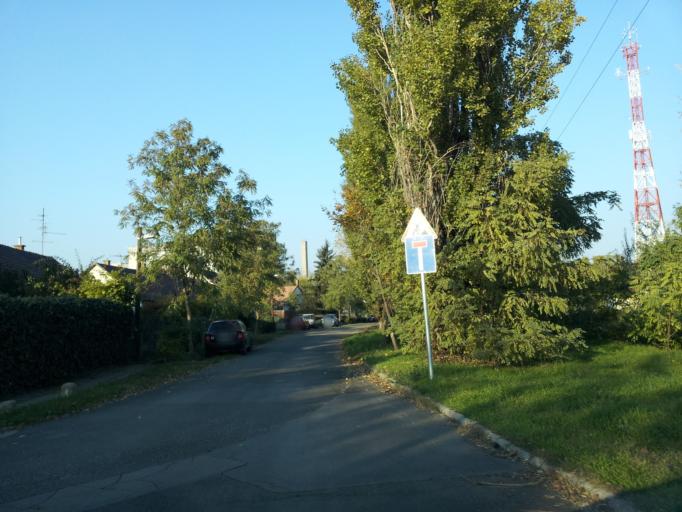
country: HU
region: Budapest
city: Budapest X. keruelet
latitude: 47.4740
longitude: 19.1681
